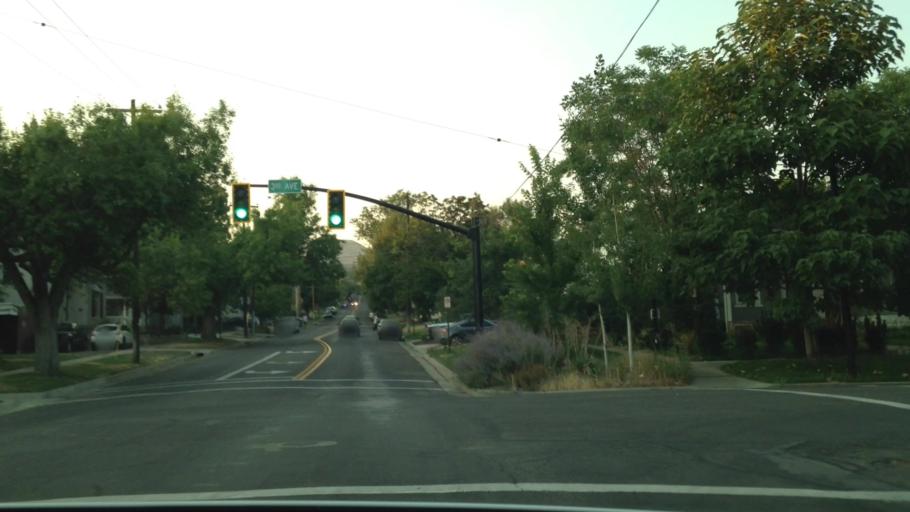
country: US
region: Utah
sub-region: Salt Lake County
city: Salt Lake City
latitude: 40.7726
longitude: -111.8775
